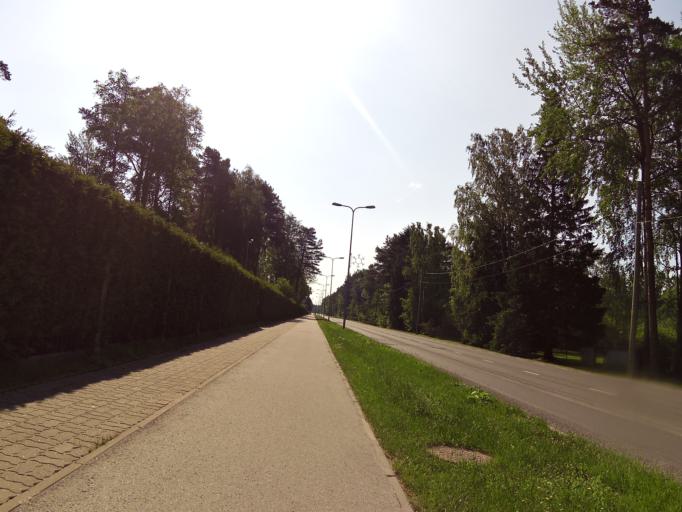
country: EE
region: Harju
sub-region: Harku vald
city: Tabasalu
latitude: 59.4468
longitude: 24.6081
